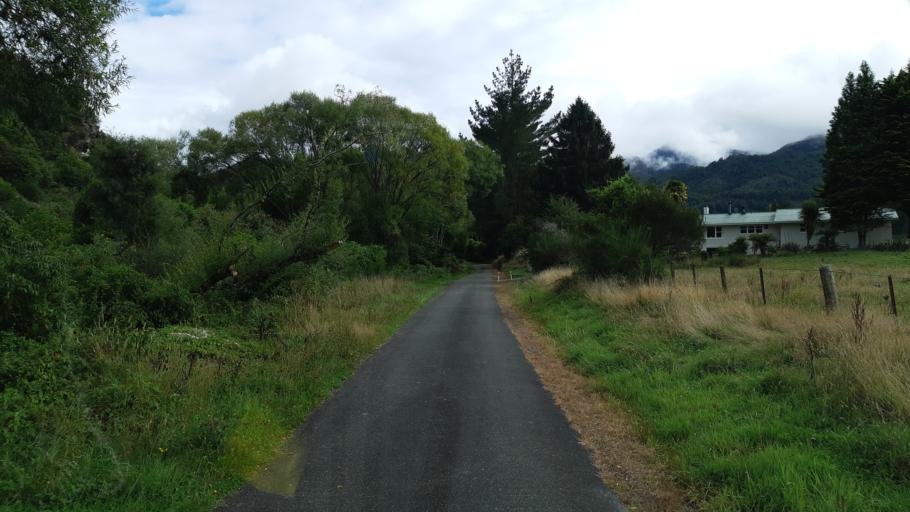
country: NZ
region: West Coast
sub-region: Buller District
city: Westport
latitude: -41.7830
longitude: 172.2759
